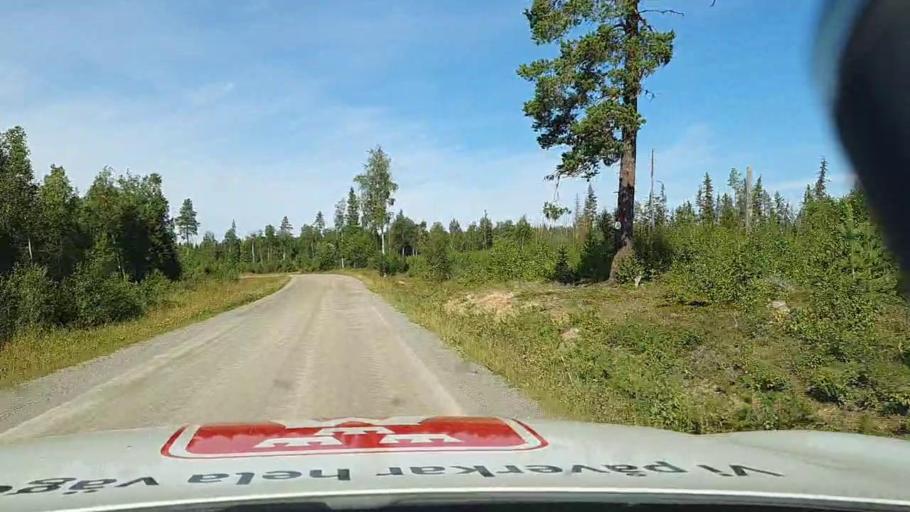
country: SE
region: Jaemtland
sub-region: Stroemsunds Kommun
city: Stroemsund
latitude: 63.7154
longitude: 15.2992
